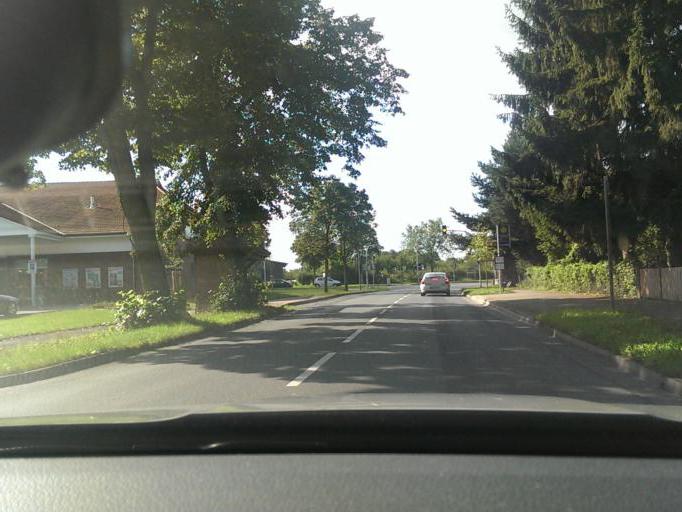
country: DE
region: Lower Saxony
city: Isernhagen Farster Bauerschaft
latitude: 52.4746
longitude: 9.8560
